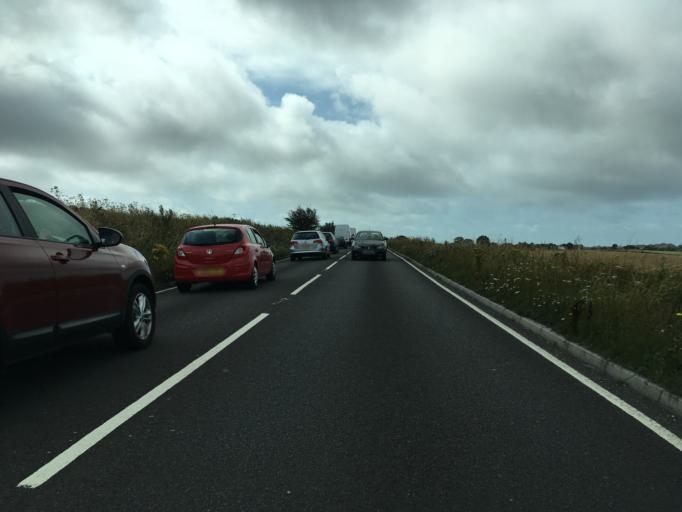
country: GB
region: England
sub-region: Brighton and Hove
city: Rottingdean
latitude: 50.8428
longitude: -0.0737
